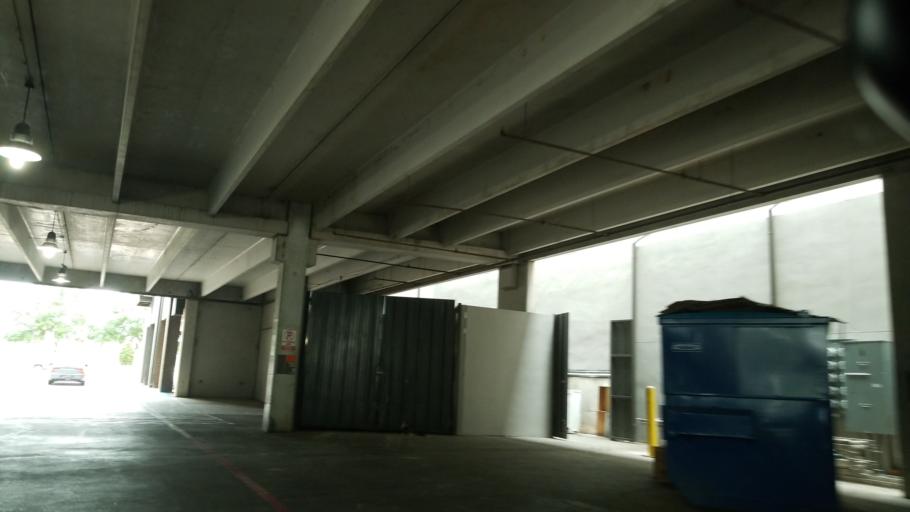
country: US
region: Texas
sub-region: Dallas County
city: Dallas
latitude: 32.8129
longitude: -96.8300
